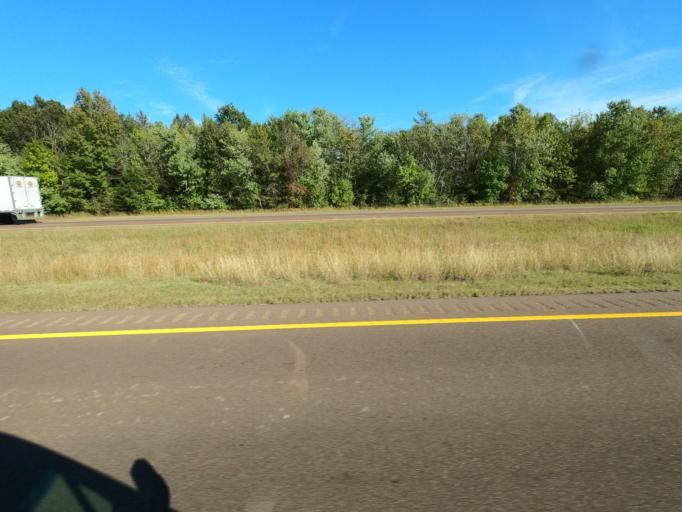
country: US
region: Tennessee
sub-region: Dyer County
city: Dyersburg
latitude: 36.0042
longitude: -89.3418
